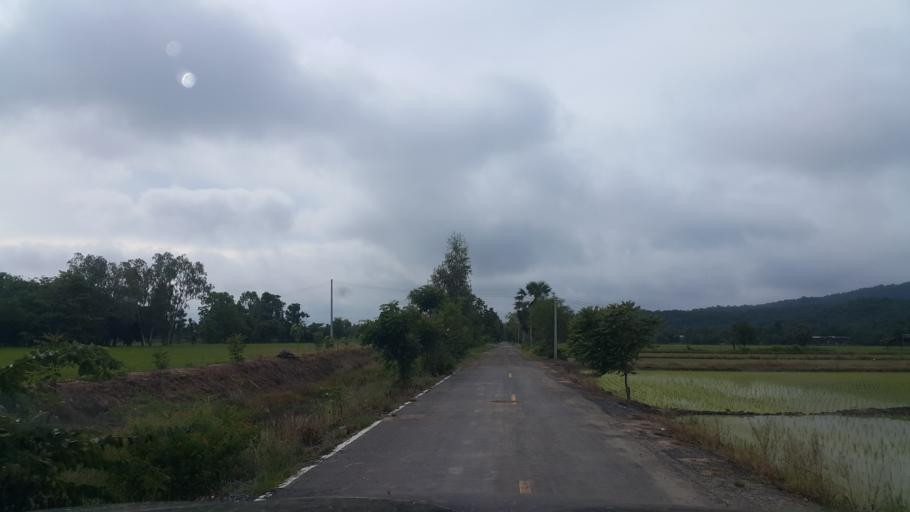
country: TH
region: Sukhothai
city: Sawankhalok
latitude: 17.3091
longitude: 99.7012
